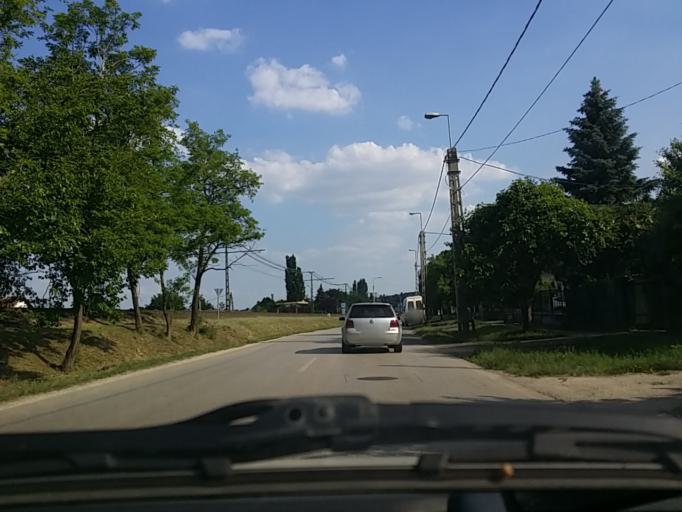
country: HU
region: Pest
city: Budakalasz
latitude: 47.6308
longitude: 19.0421
